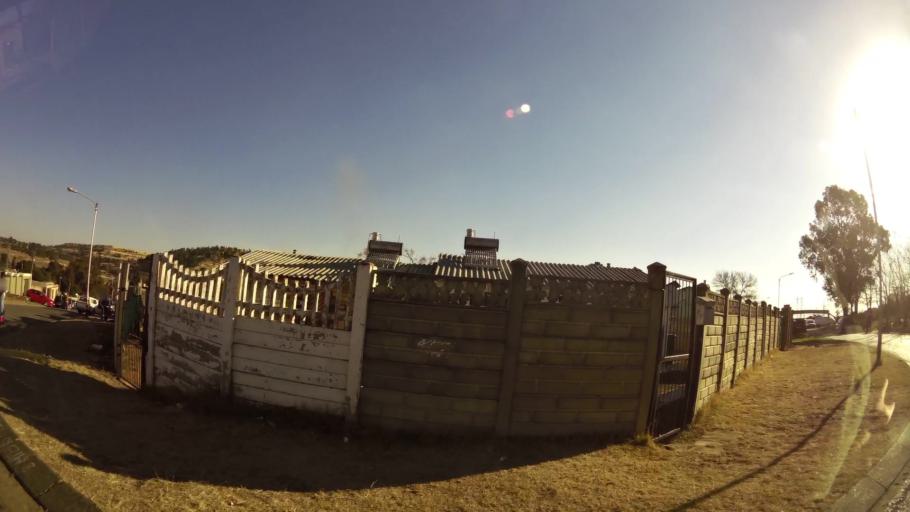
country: ZA
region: Gauteng
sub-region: City of Johannesburg Metropolitan Municipality
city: Johannesburg
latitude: -26.2180
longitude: 27.9811
